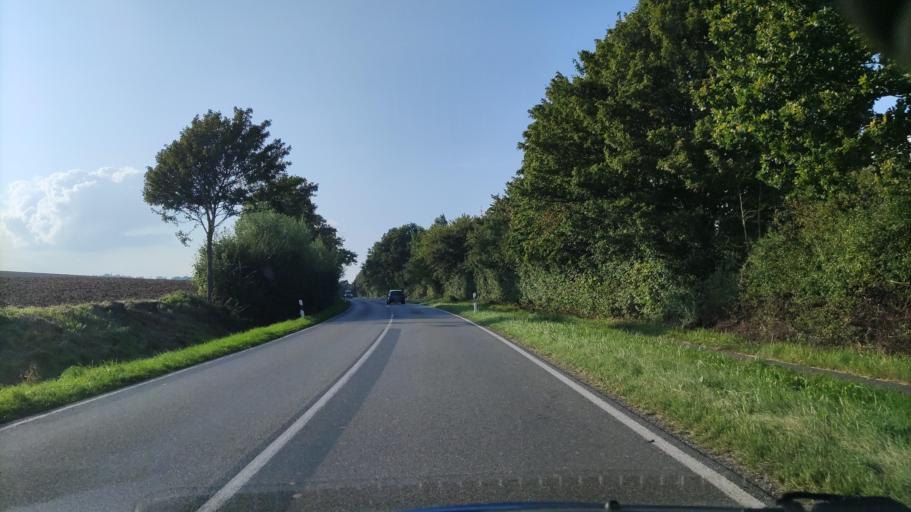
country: DE
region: Schleswig-Holstein
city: Ahrensbok
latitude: 53.9818
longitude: 10.5857
